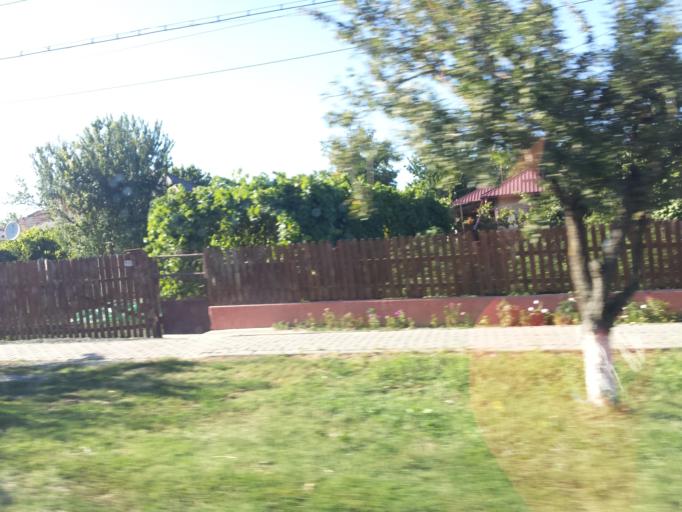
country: RO
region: Ialomita
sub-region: Comuna Ograda
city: Ograda
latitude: 44.6130
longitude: 27.5650
